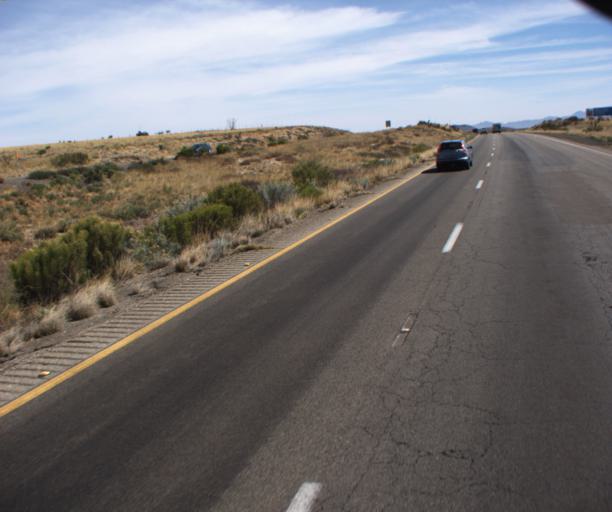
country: US
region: Arizona
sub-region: Cochise County
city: Saint David
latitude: 32.0829
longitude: -110.0489
